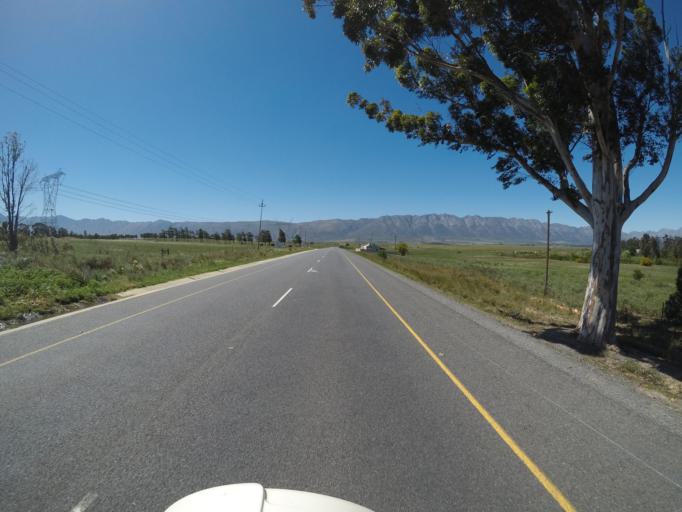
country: ZA
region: Western Cape
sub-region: Cape Winelands District Municipality
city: Ceres
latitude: -33.3094
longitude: 19.1044
